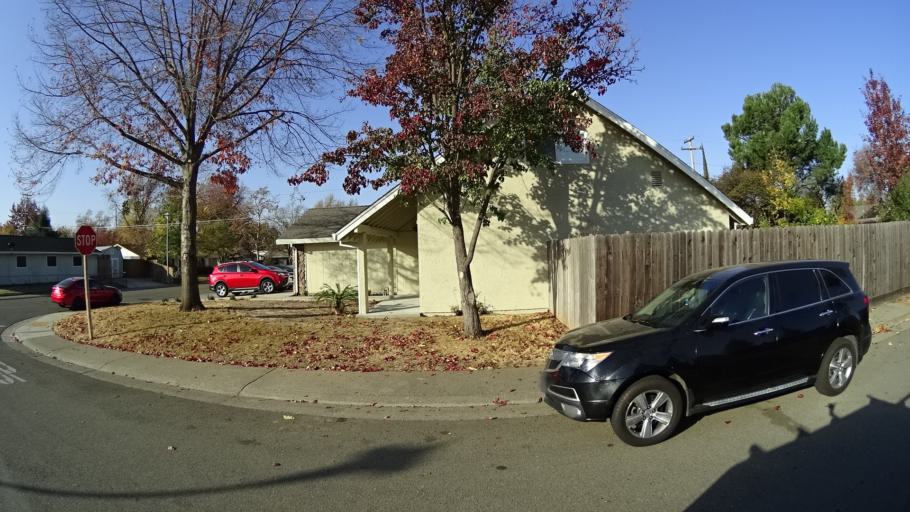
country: US
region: California
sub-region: Sacramento County
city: Citrus Heights
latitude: 38.6990
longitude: -121.2655
